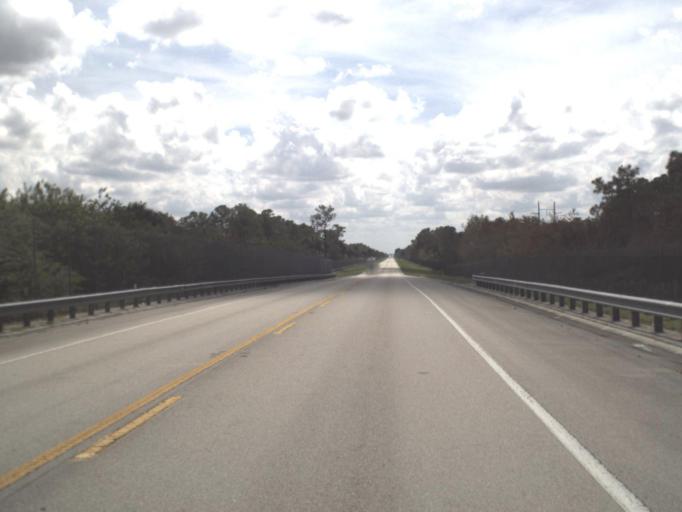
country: US
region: Florida
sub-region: Collier County
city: Immokalee
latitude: 26.1953
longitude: -81.3460
